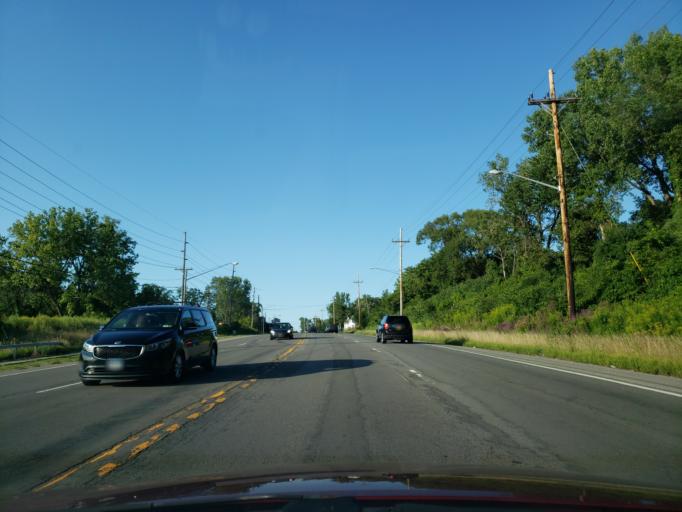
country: US
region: New York
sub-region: Monroe County
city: Brighton
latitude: 43.1761
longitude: -77.5115
